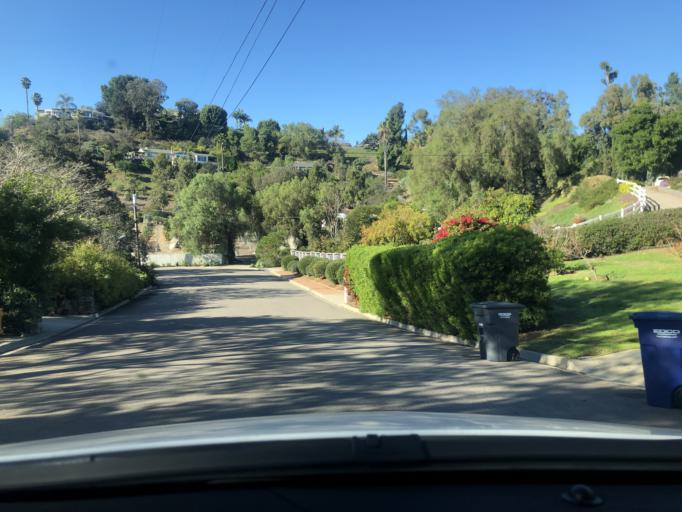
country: US
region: California
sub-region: San Diego County
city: Rancho San Diego
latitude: 32.7681
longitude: -116.9437
